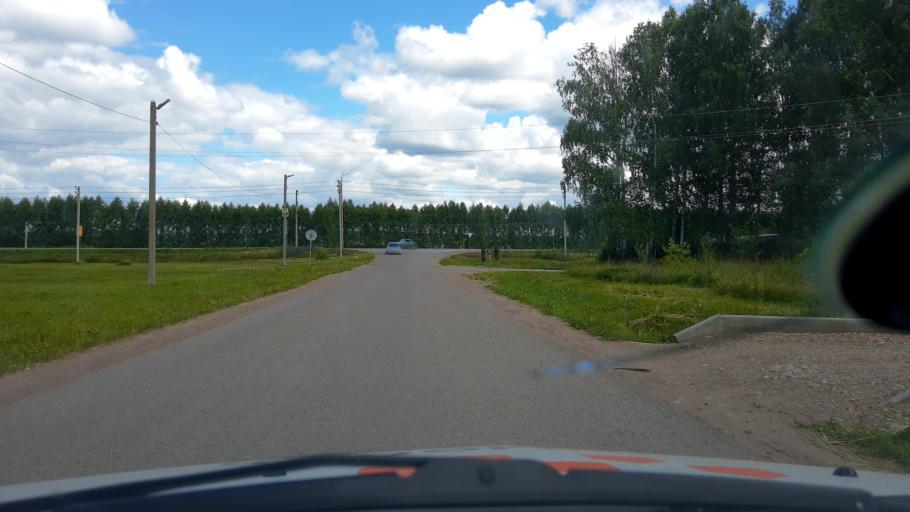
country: RU
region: Bashkortostan
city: Blagoveshchensk
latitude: 55.0525
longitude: 55.9667
